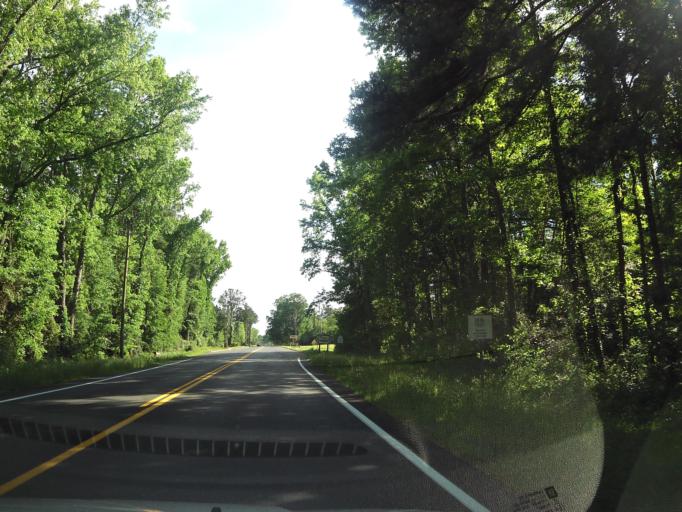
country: US
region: South Carolina
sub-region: Allendale County
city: Fairfax
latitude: 32.9737
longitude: -81.2313
